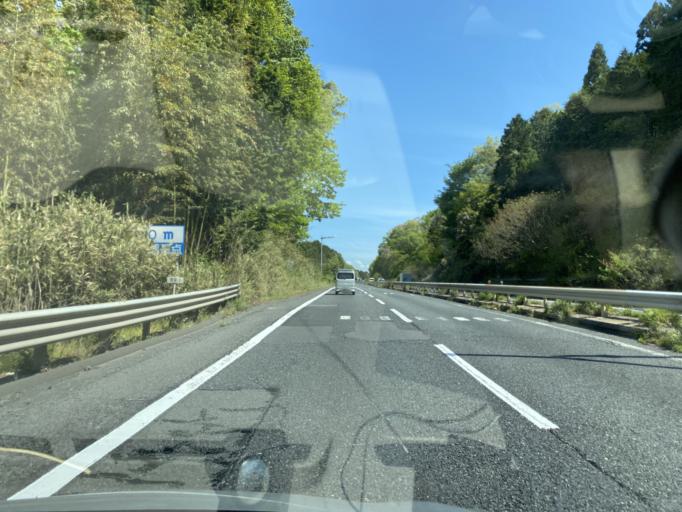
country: JP
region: Mie
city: Nabari
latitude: 34.6641
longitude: 136.0330
